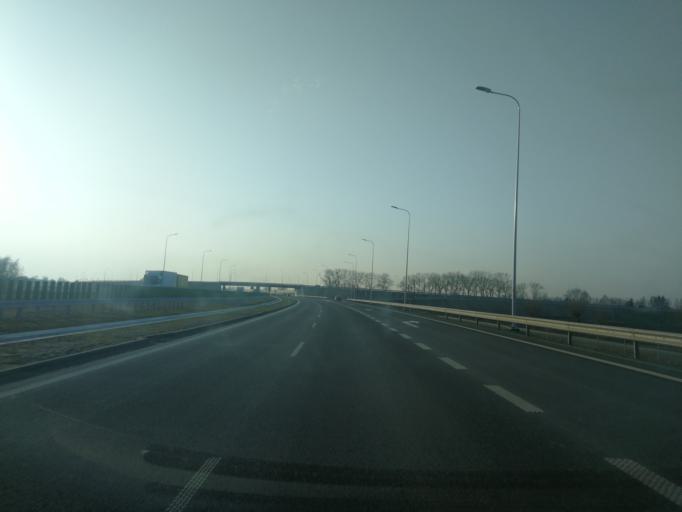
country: PL
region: Warmian-Masurian Voivodeship
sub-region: Powiat elblaski
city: Elblag
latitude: 54.1632
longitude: 19.3511
